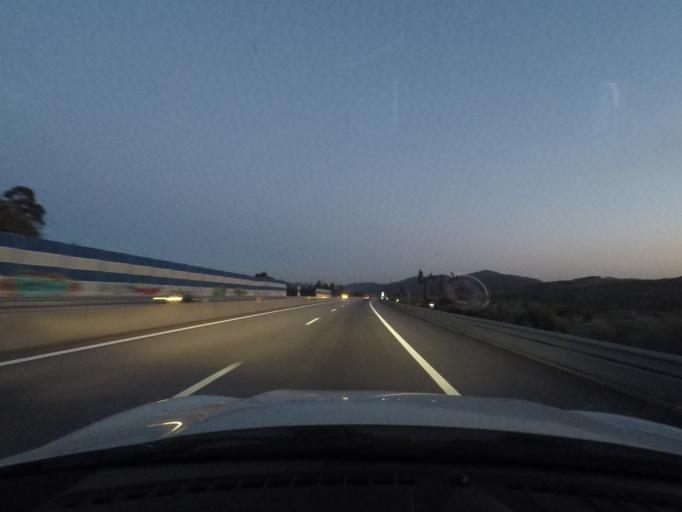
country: PT
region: Porto
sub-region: Paredes
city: Recarei
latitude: 41.1501
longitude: -8.4324
